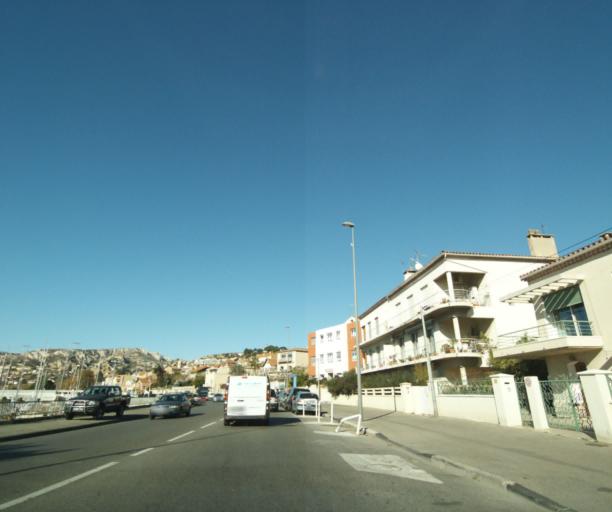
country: FR
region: Provence-Alpes-Cote d'Azur
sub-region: Departement des Bouches-du-Rhone
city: Marseille 16
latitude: 43.3584
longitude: 5.3187
